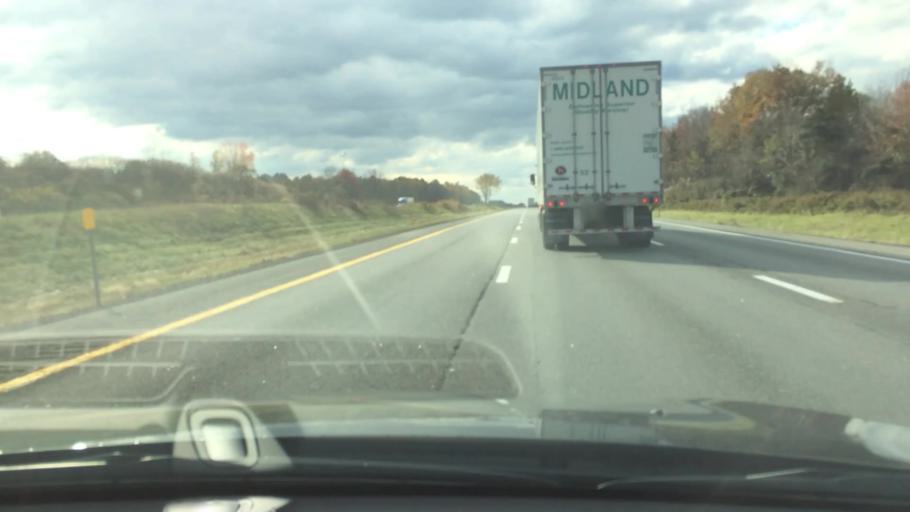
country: US
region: New York
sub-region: Saratoga County
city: Ballston Spa
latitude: 42.9843
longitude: -73.8034
